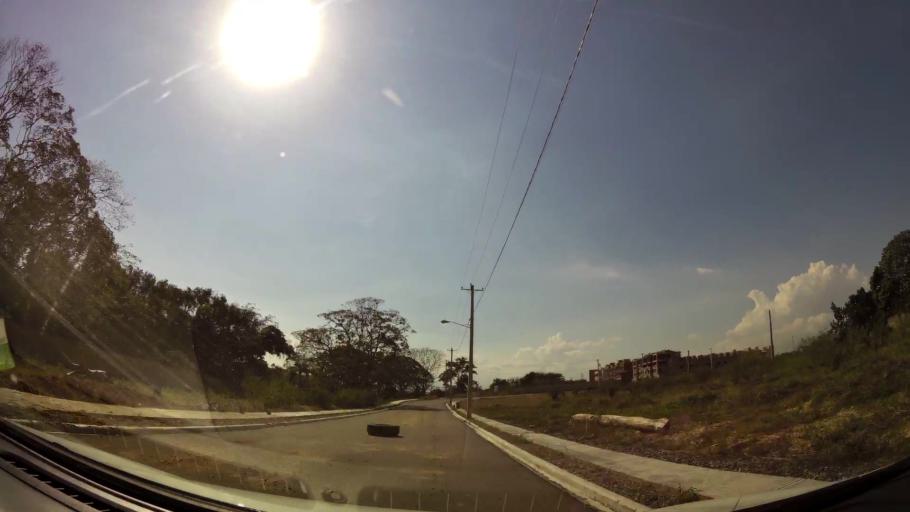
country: DO
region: Nacional
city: Bella Vista
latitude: 18.4566
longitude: -69.9795
